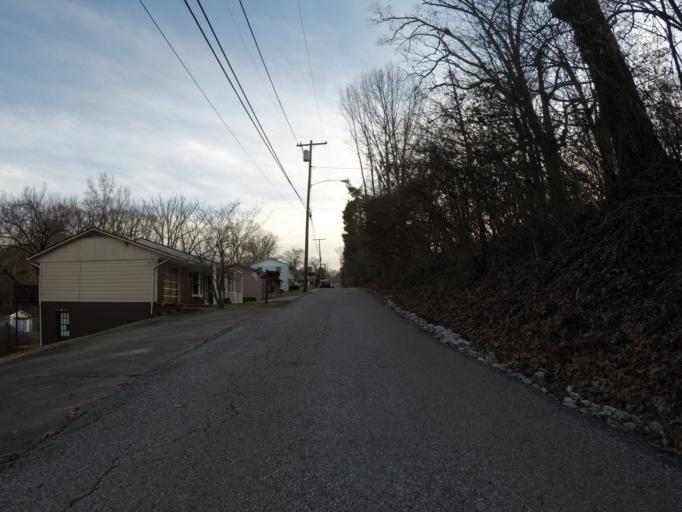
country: US
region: West Virginia
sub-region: Cabell County
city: Huntington
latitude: 38.4062
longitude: -82.3908
